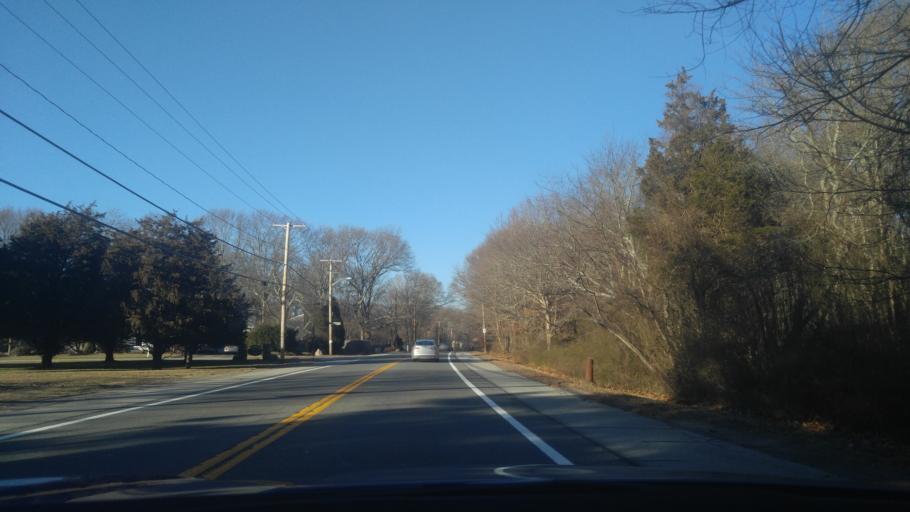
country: US
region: Rhode Island
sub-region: Washington County
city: North Kingstown
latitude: 41.4941
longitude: -71.4379
